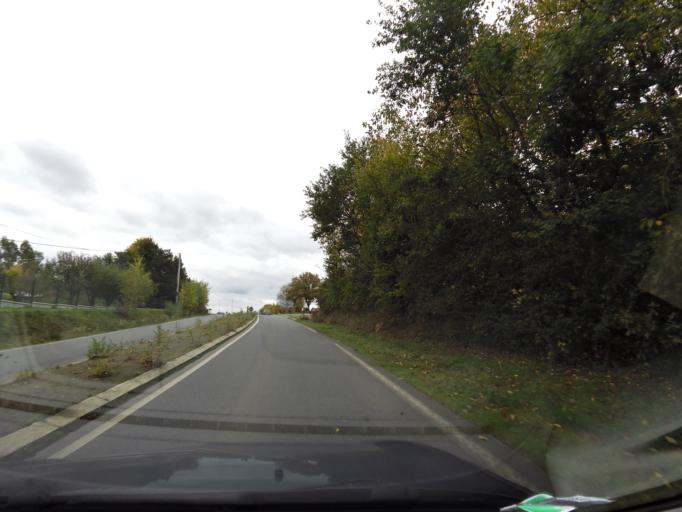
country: FR
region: Brittany
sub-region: Departement d'Ille-et-Vilaine
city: Corps-Nuds
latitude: 47.9903
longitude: -1.5920
